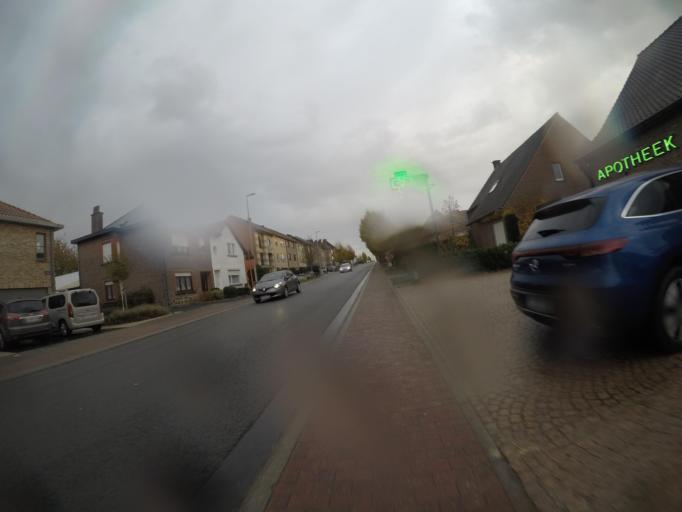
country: BE
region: Flanders
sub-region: Provincie Vlaams-Brabant
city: Ledeberg
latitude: 50.8594
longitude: 4.1147
